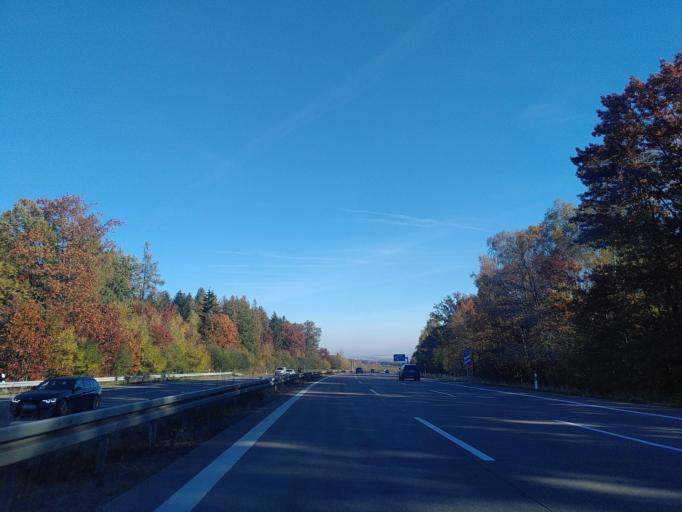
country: DE
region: Saxony
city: Limbach-Oberfrohna
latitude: 50.8436
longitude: 12.8005
